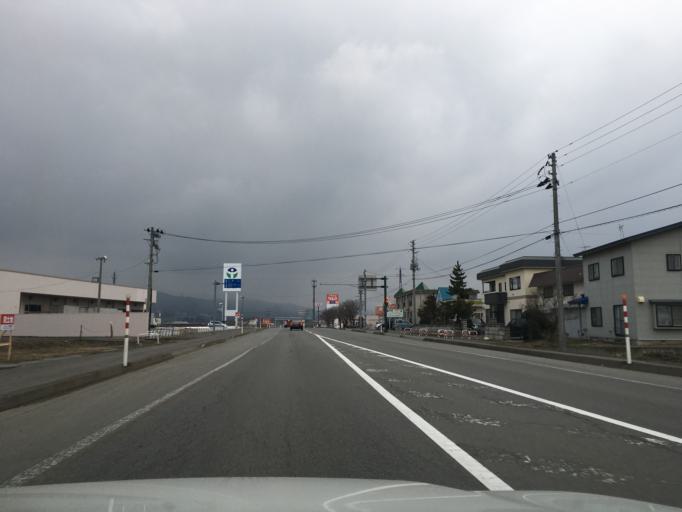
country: JP
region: Aomori
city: Kuroishi
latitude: 40.5834
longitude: 140.5687
